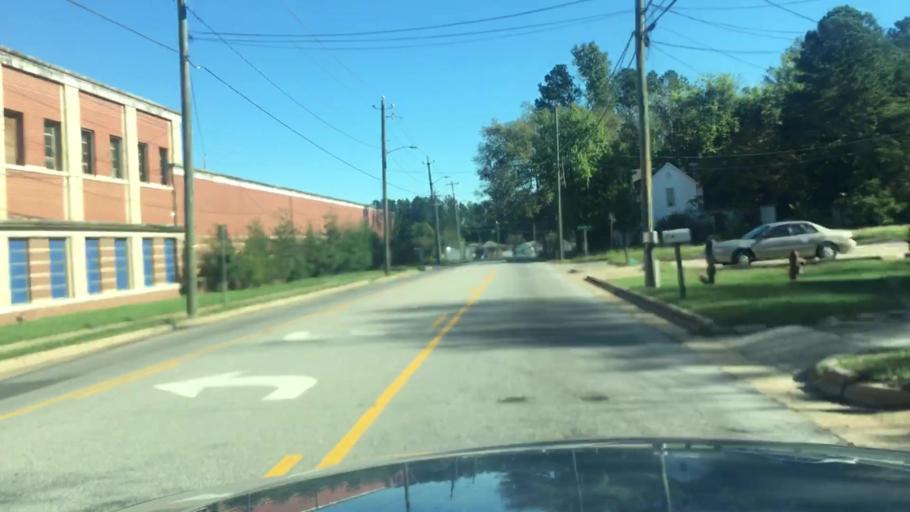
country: US
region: North Carolina
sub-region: Cumberland County
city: Fayetteville
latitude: 35.0361
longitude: -78.8902
